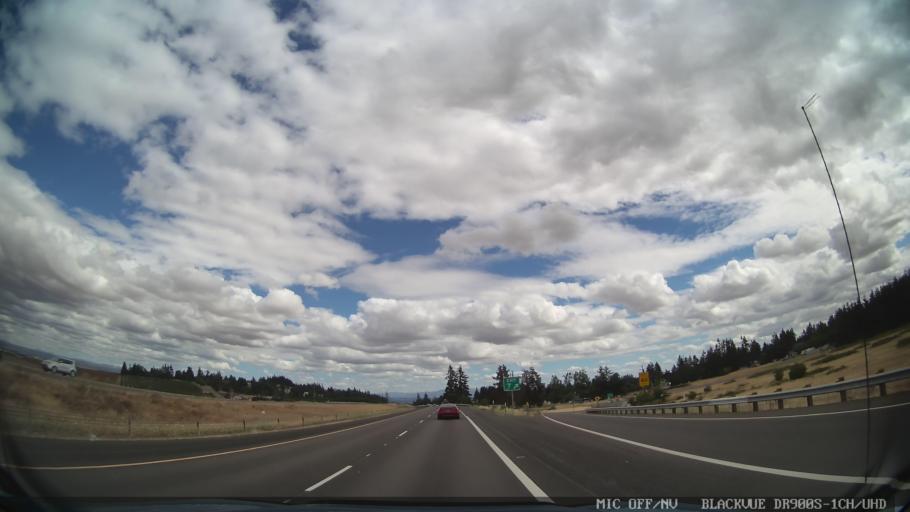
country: US
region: Oregon
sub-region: Marion County
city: Aumsville
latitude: 44.8740
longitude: -122.9047
